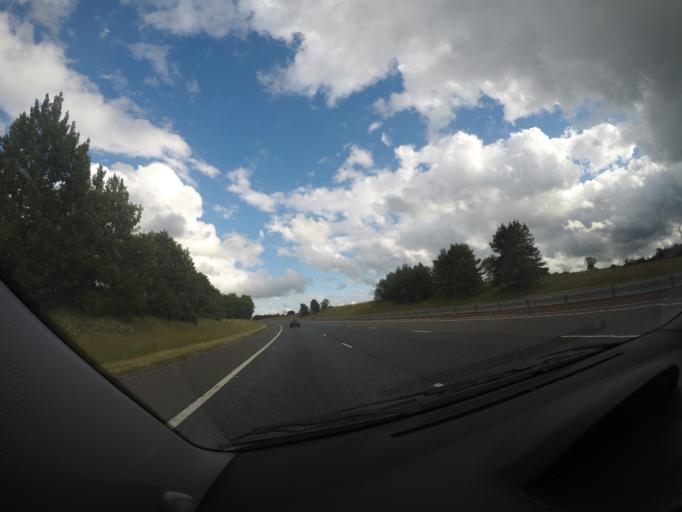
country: GB
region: Scotland
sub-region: Dumfries and Galloway
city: Lochmaben
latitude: 55.1779
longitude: -3.4033
